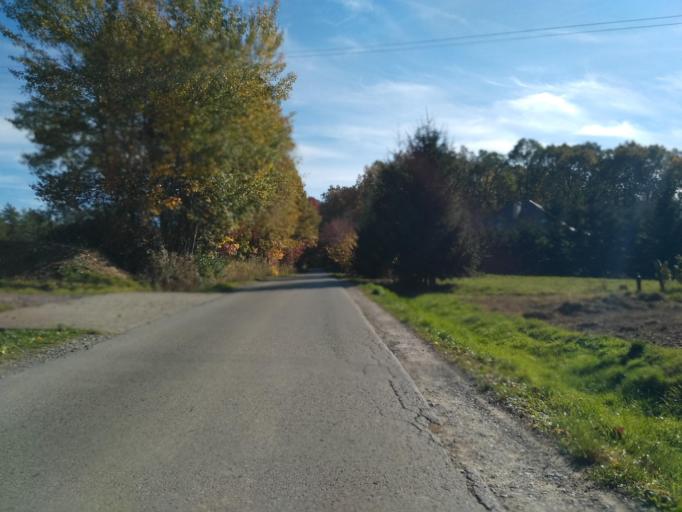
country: PL
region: Subcarpathian Voivodeship
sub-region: Powiat ropczycko-sedziszowski
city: Iwierzyce
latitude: 50.0482
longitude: 21.7707
